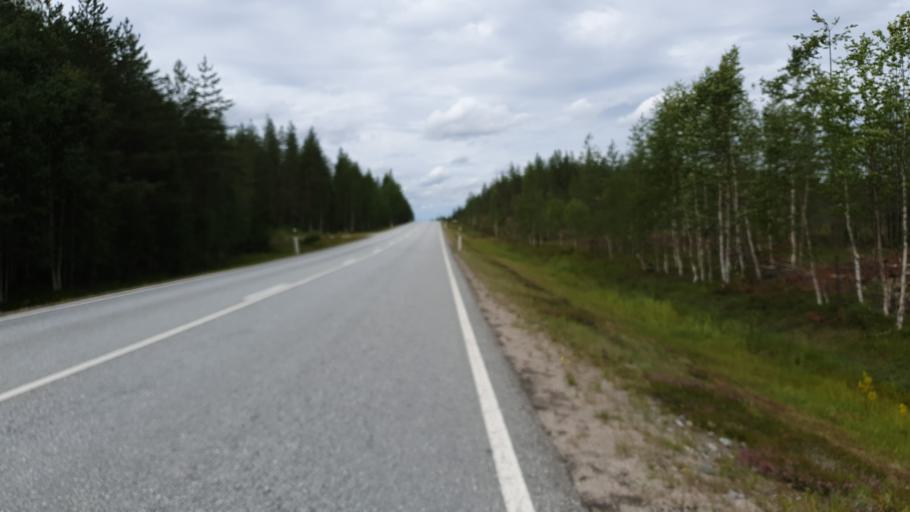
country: FI
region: Kainuu
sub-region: Kehys-Kainuu
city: Kuhmo
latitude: 64.4911
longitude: 29.8290
